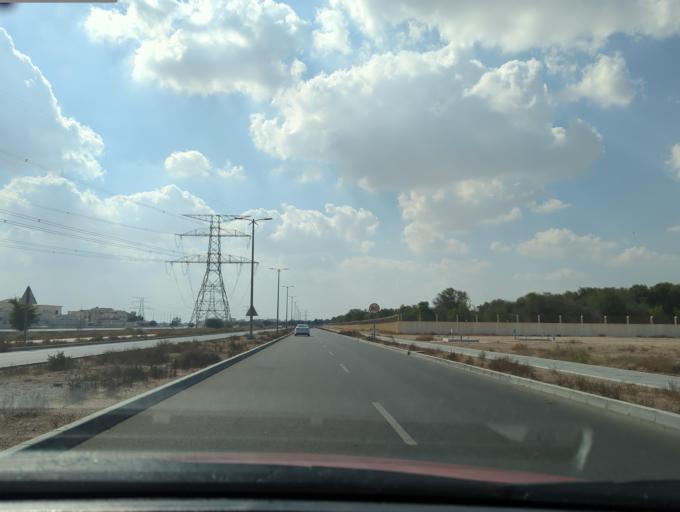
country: AE
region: Abu Dhabi
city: Al Ain
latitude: 24.1715
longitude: 55.6578
